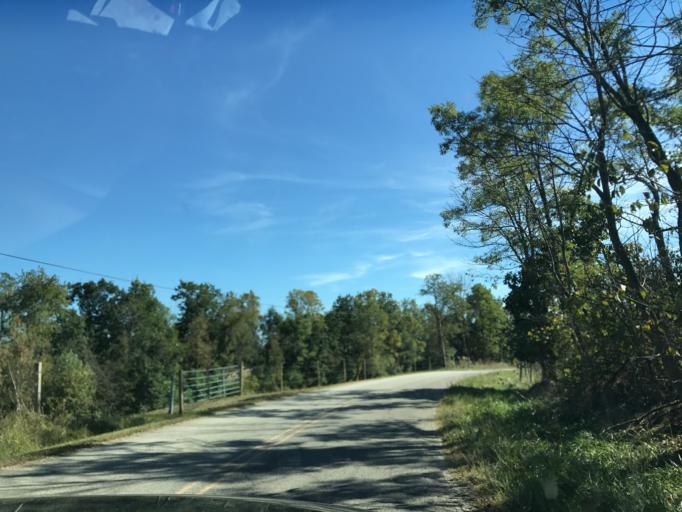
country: US
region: Ohio
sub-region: Belmont County
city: Barnesville
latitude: 40.0551
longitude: -81.2884
